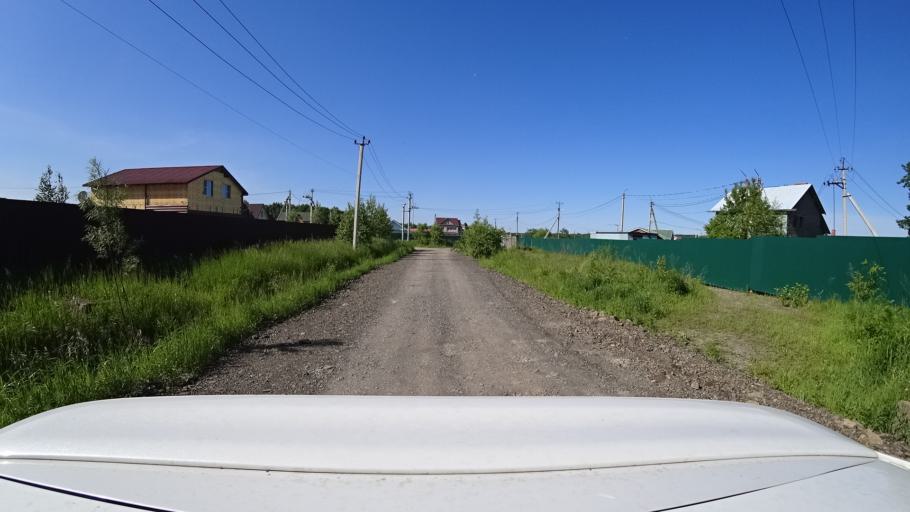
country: RU
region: Khabarovsk Krai
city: Topolevo
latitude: 48.5487
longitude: 135.1827
